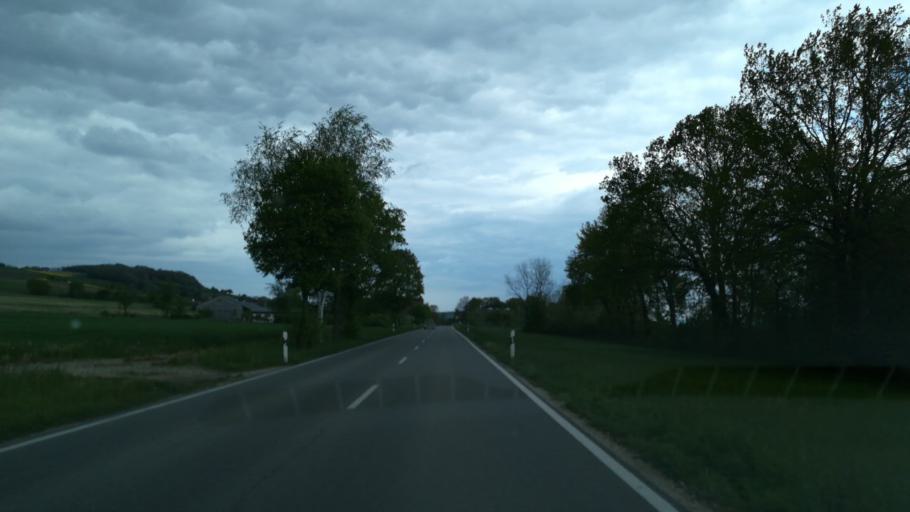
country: CH
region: Schaffhausen
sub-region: Bezirk Reiat
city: Thayngen
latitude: 47.7788
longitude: 8.7204
